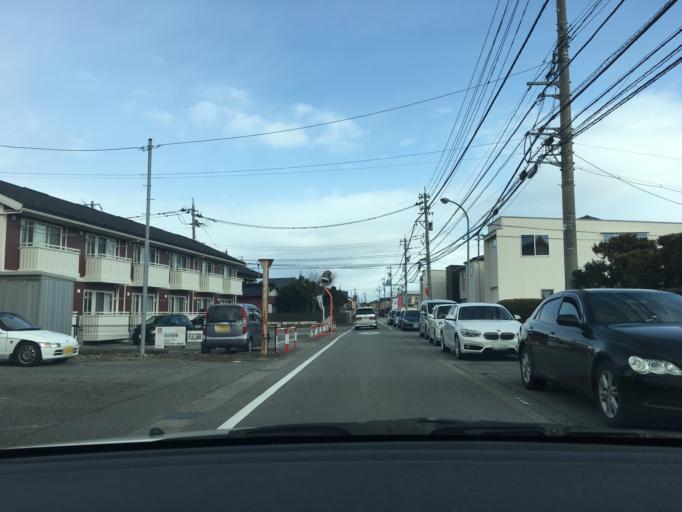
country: JP
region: Toyama
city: Toyama-shi
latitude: 36.6660
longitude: 137.1702
